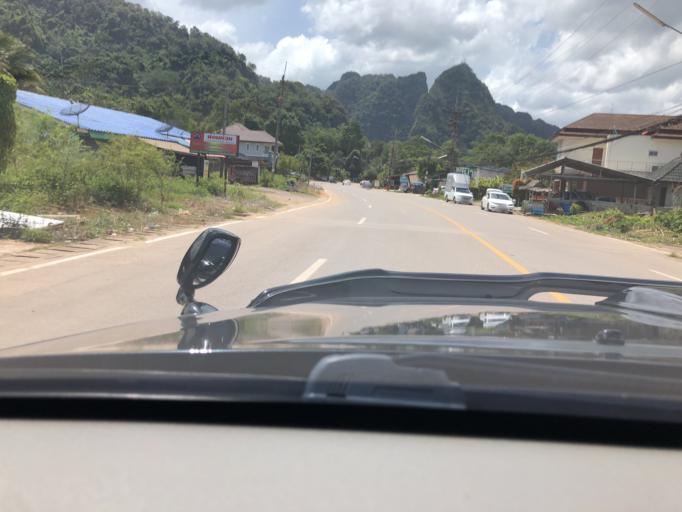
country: TH
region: Krabi
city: Krabi
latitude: 8.1134
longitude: 98.9233
